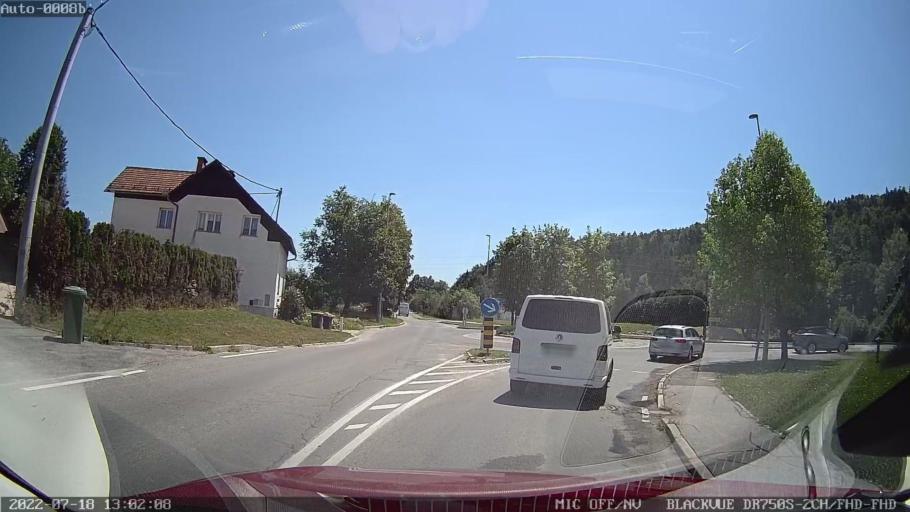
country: SI
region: Brezovica
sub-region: Opstina Ljubljana-Vic-Rudnik
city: Brezovica pri Ljubljani
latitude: 46.0530
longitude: 14.4197
